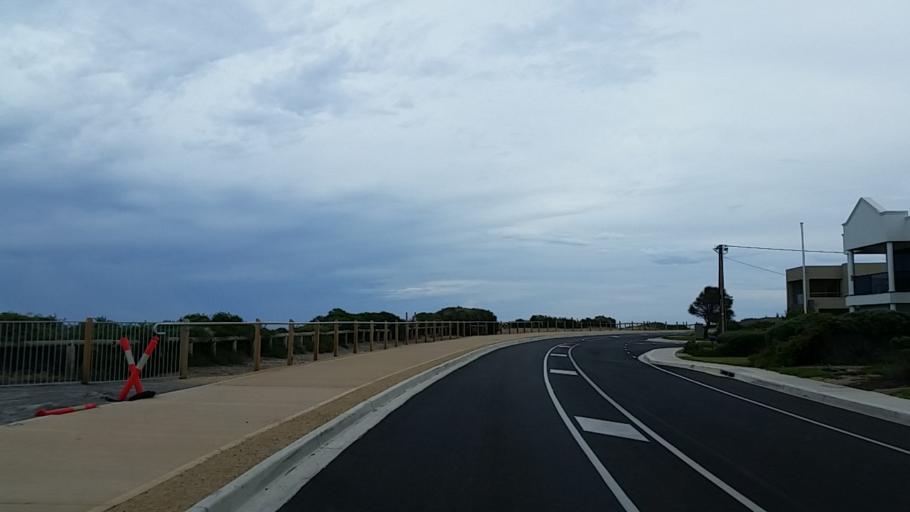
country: AU
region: South Australia
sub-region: Onkaparinga
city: Port Willunga
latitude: -35.2780
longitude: 138.4430
